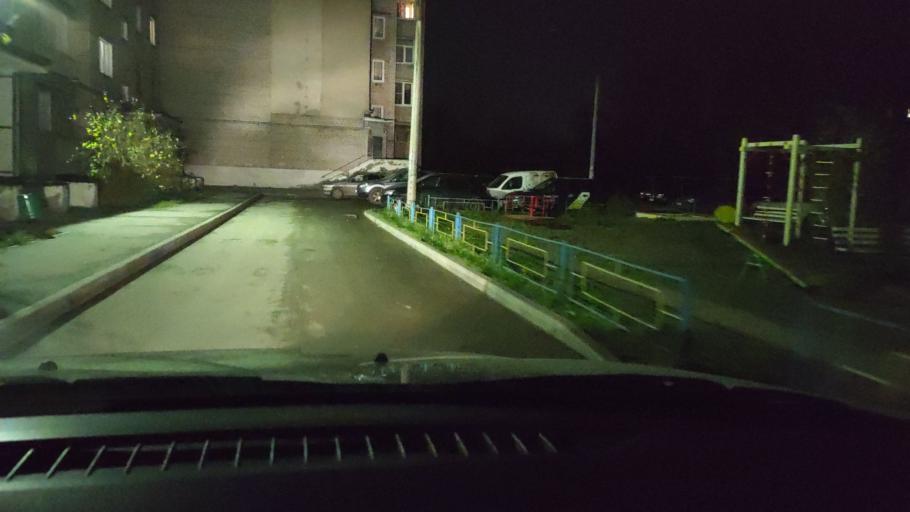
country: RU
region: Perm
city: Kondratovo
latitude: 58.0033
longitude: 56.1091
